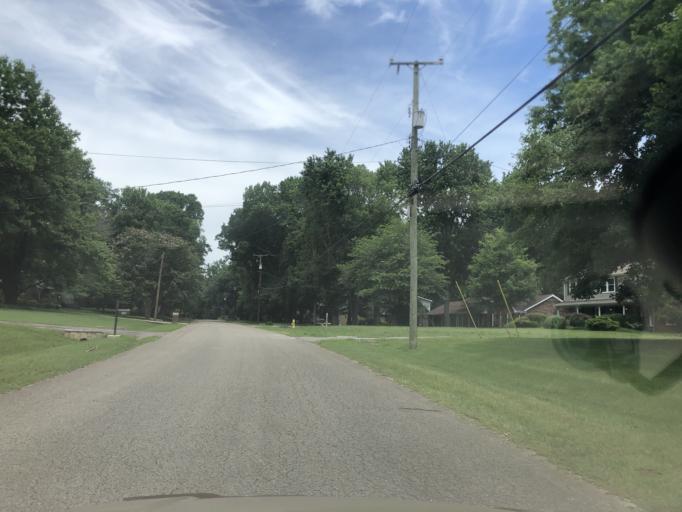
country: US
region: Tennessee
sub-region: Davidson County
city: Lakewood
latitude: 36.2589
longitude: -86.5917
